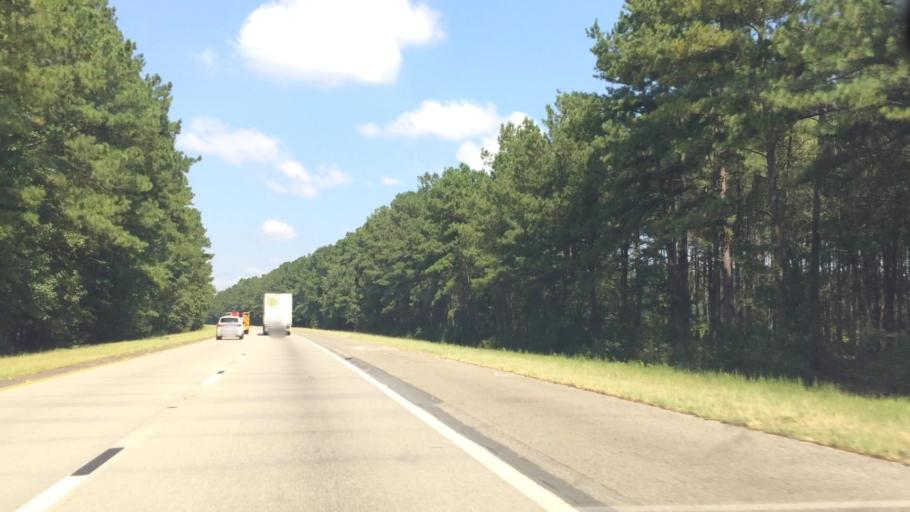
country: US
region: South Carolina
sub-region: Colleton County
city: Walterboro
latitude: 33.0213
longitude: -80.6653
